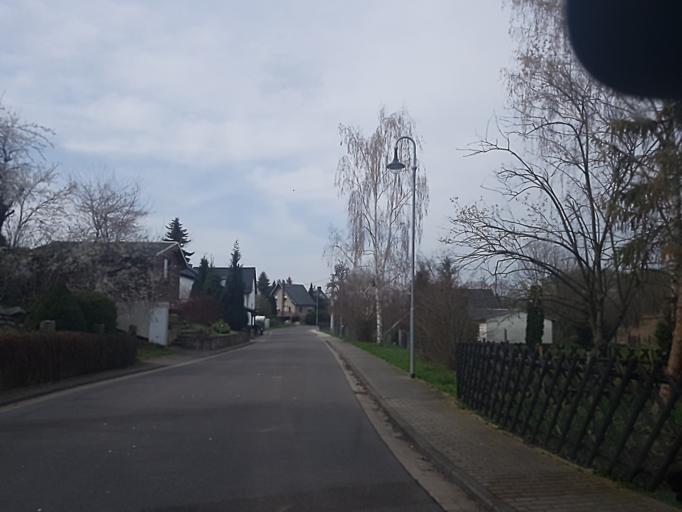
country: DE
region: Saxony
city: Bockelwitz
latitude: 51.2103
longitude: 12.9826
